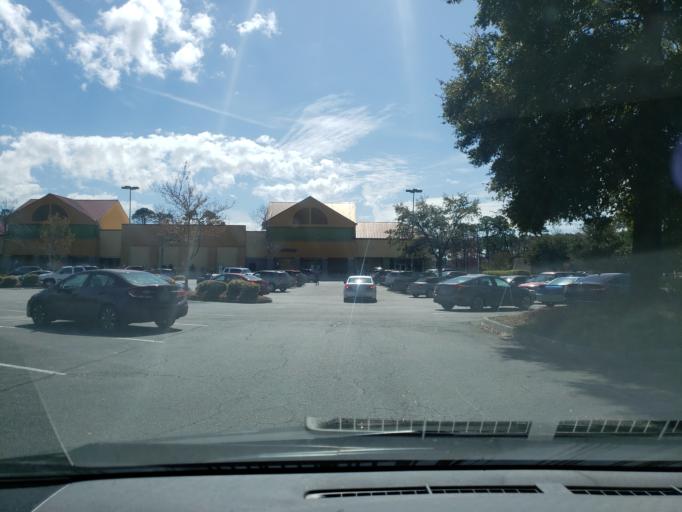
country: US
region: Georgia
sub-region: Chatham County
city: Whitemarsh Island
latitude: 32.0426
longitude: -81.0074
